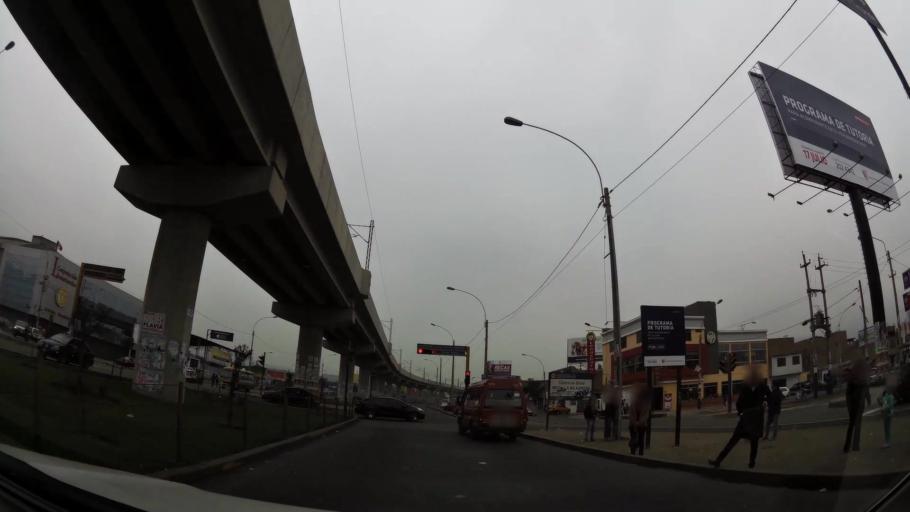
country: PE
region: Lima
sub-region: Lima
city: Independencia
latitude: -11.9783
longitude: -77.0039
